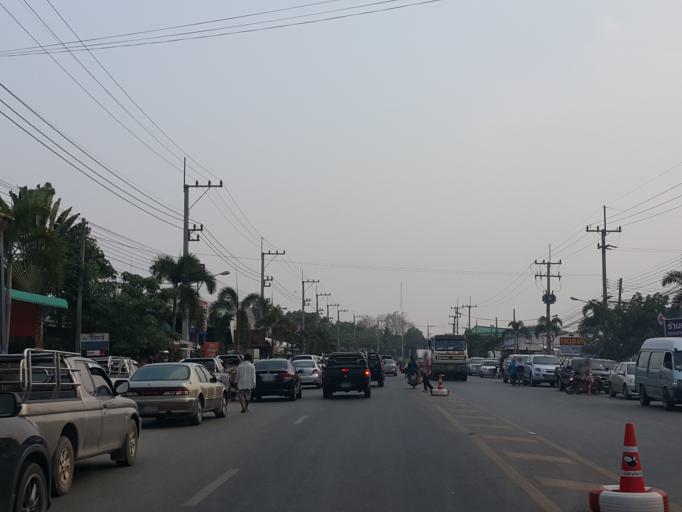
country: TH
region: Uthai Thani
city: Huai Khot
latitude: 15.1813
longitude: 99.6971
